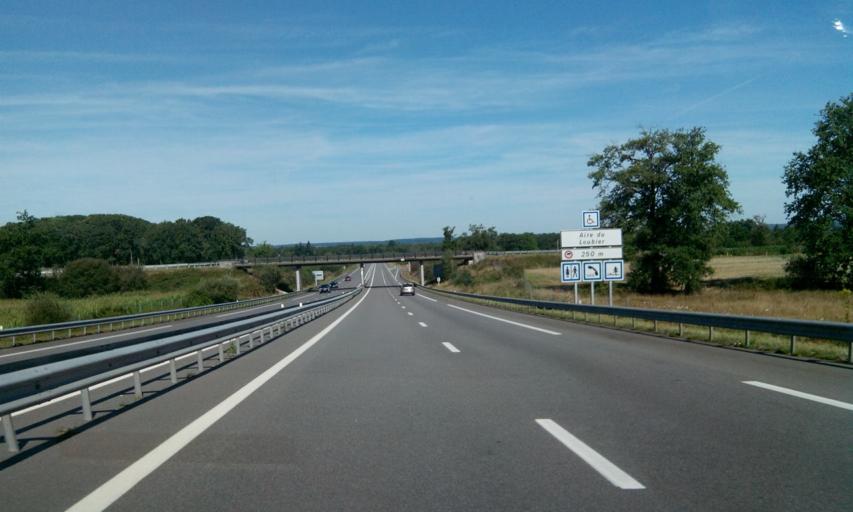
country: FR
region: Limousin
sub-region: Departement de la Haute-Vienne
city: Saint-Victurnien
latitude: 45.9003
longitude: 1.0235
